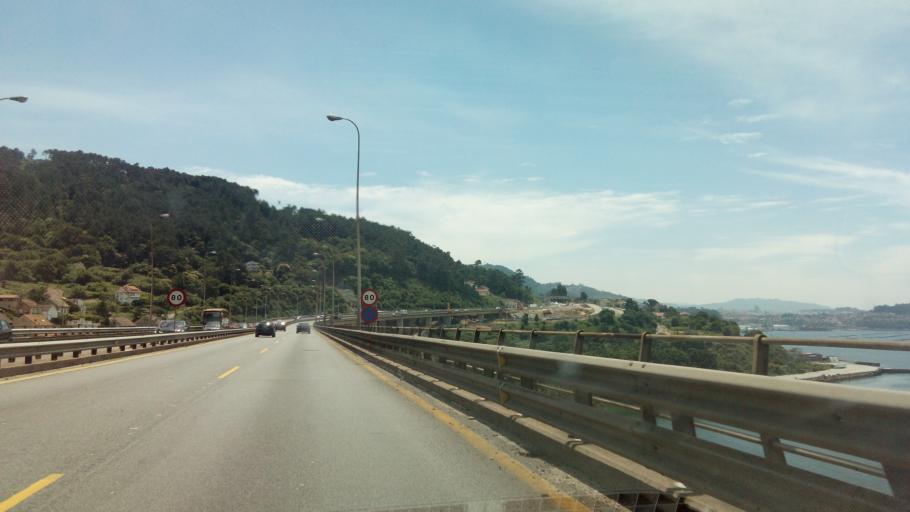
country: ES
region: Galicia
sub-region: Provincia de Pontevedra
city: Redondela
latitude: 42.2848
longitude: -8.6610
